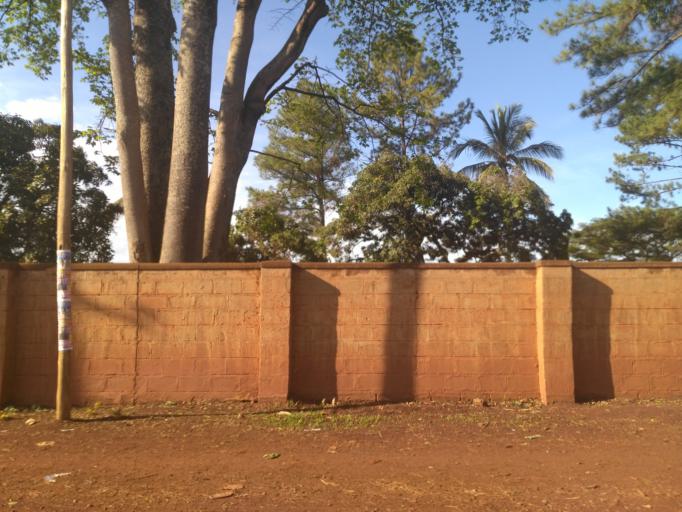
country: UG
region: Eastern Region
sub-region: Jinja District
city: Jinja
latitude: 0.4545
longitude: 33.1877
